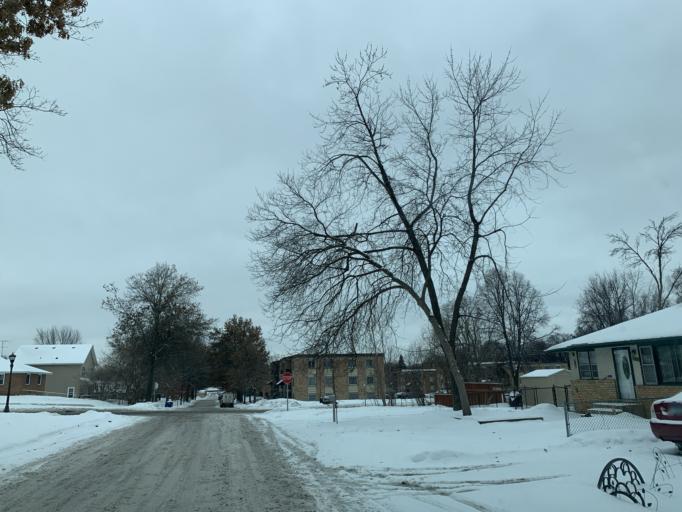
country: US
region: Minnesota
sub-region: Ramsey County
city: Little Canada
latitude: 44.9903
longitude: -93.1085
